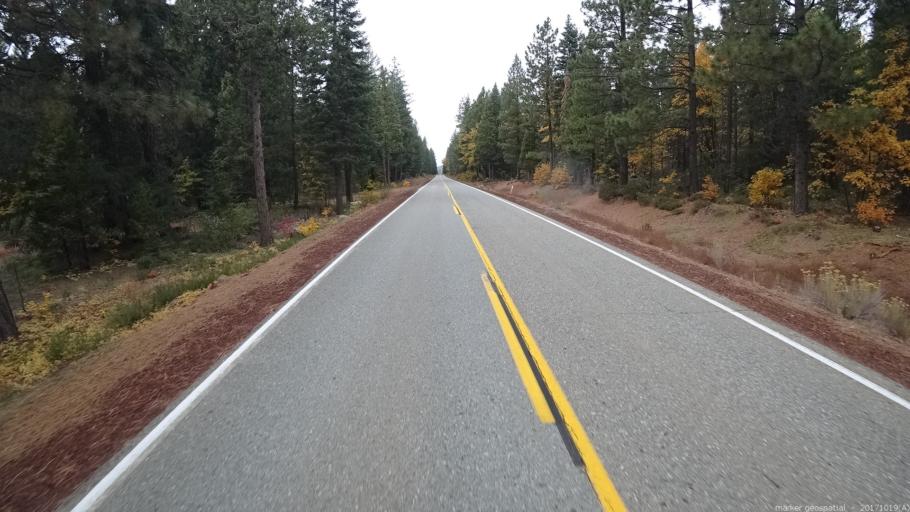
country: US
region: California
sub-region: Shasta County
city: Burney
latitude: 41.1411
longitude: -121.6310
